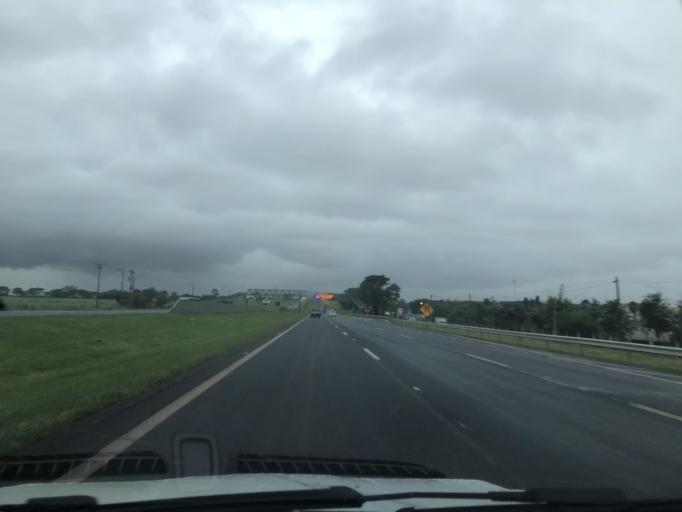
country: BR
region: Sao Paulo
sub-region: Jardinopolis
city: Jardinopolis
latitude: -21.0864
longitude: -47.7992
